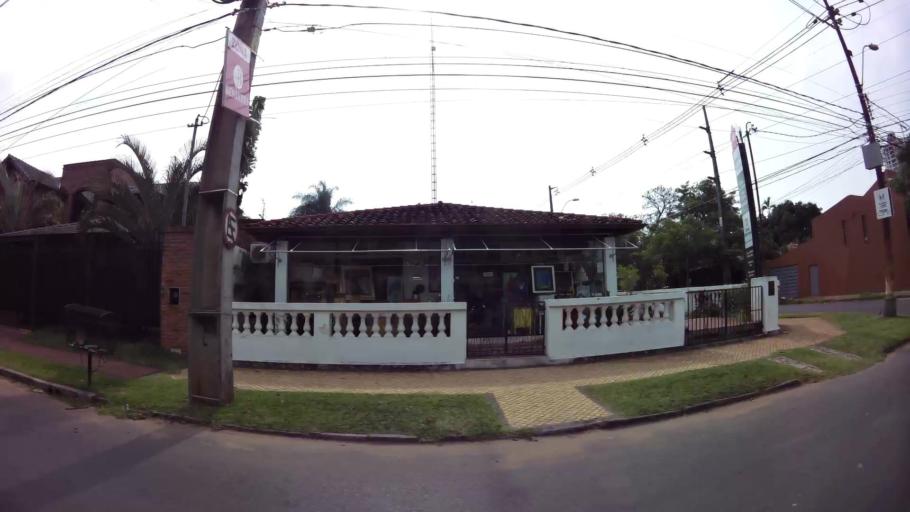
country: PY
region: Central
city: Fernando de la Mora
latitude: -25.2908
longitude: -57.5564
